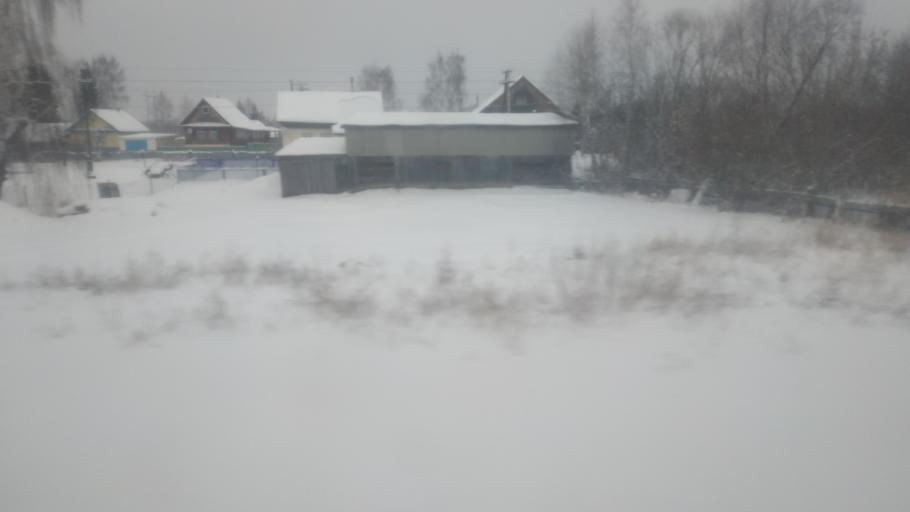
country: RU
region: Bashkortostan
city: Yanaul
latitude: 56.2534
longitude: 54.7165
